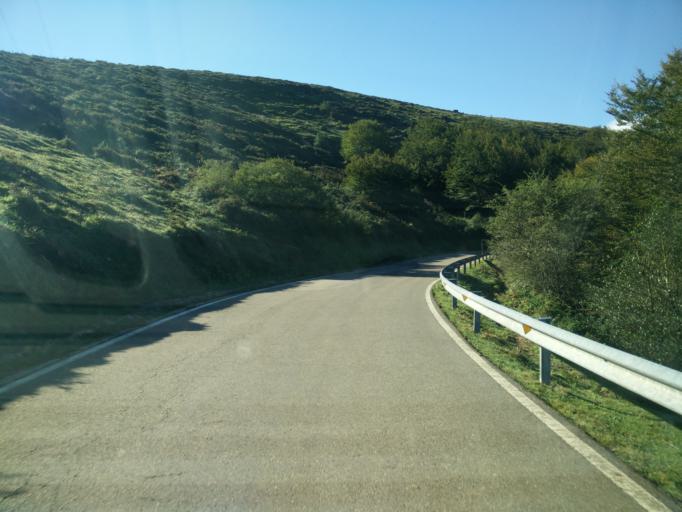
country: ES
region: Cantabria
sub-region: Provincia de Cantabria
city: San Pedro del Romeral
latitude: 43.0412
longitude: -3.8508
